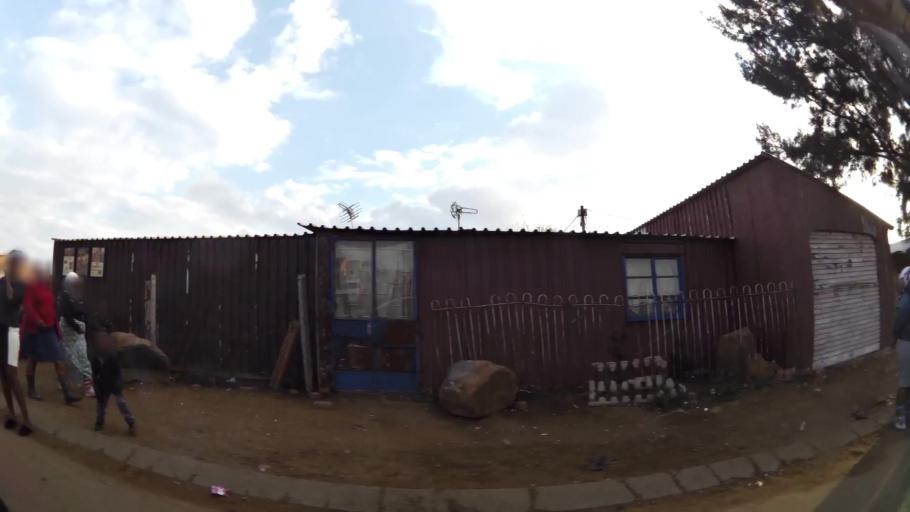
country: ZA
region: Gauteng
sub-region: City of Johannesburg Metropolitan Municipality
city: Orange Farm
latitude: -26.5919
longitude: 27.8232
